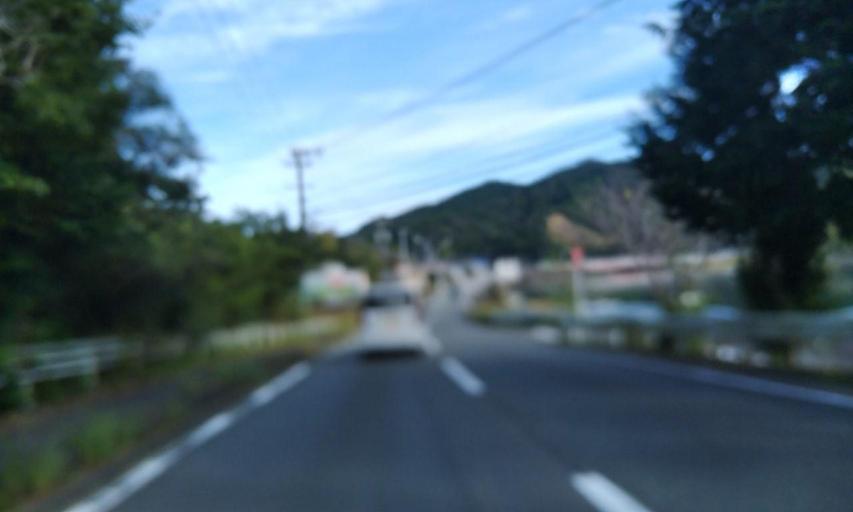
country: JP
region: Mie
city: Ise
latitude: 34.3447
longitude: 136.7241
